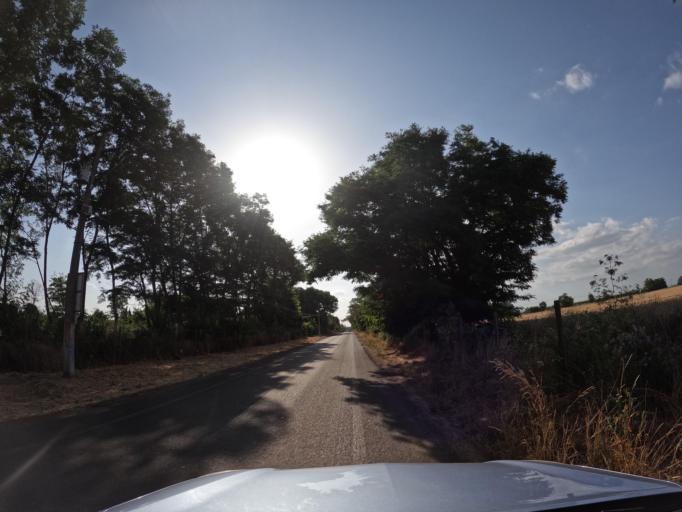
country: CL
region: Maule
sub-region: Provincia de Curico
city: Molina
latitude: -35.2603
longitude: -71.2476
